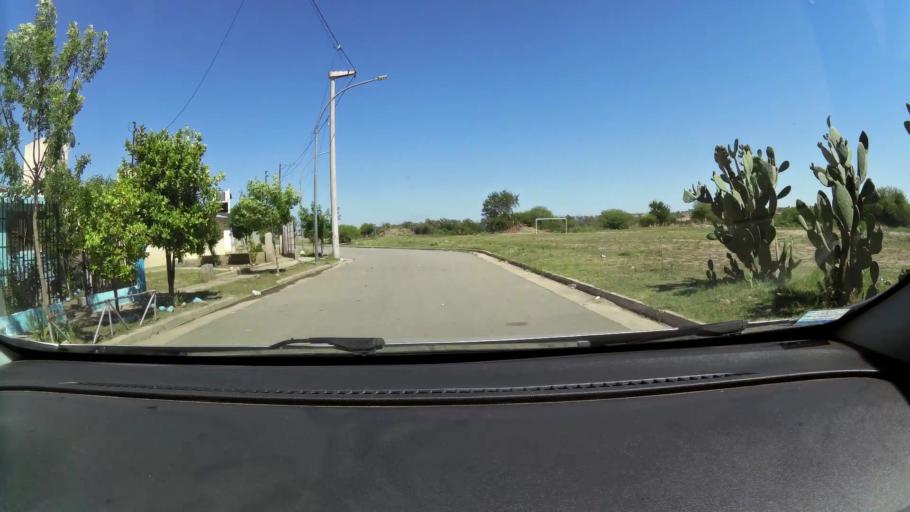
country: AR
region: Cordoba
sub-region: Departamento de Capital
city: Cordoba
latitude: -31.4078
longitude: -64.1355
